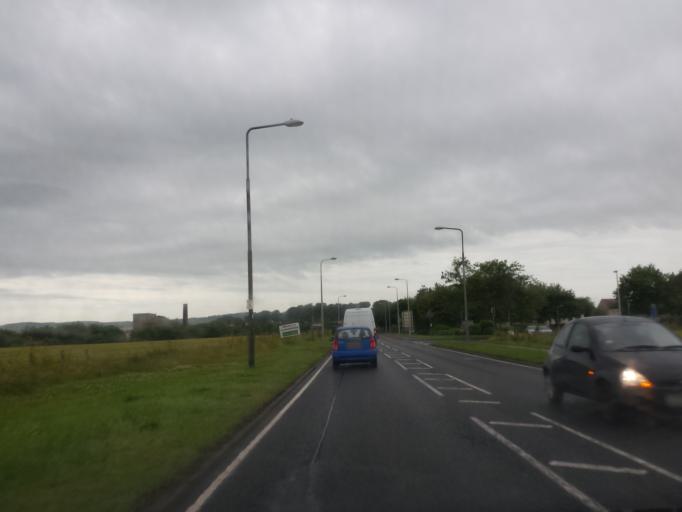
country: GB
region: Scotland
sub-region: Fife
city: Leuchars
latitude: 56.3706
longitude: -2.8896
